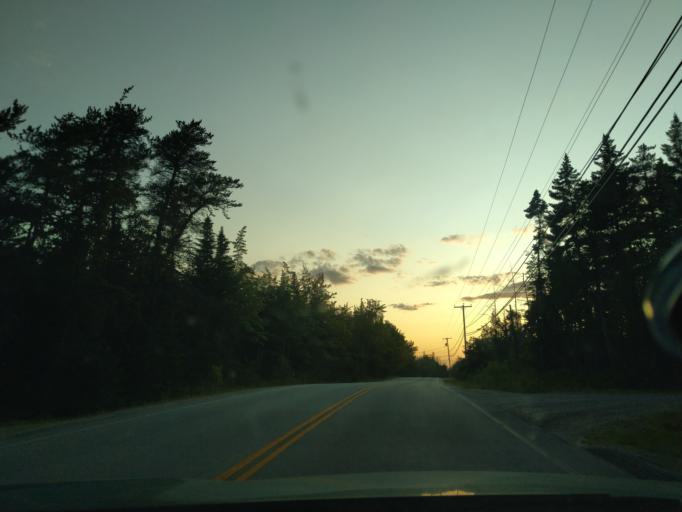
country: US
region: Maine
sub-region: Hancock County
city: Gouldsboro
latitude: 44.3921
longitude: -68.0540
